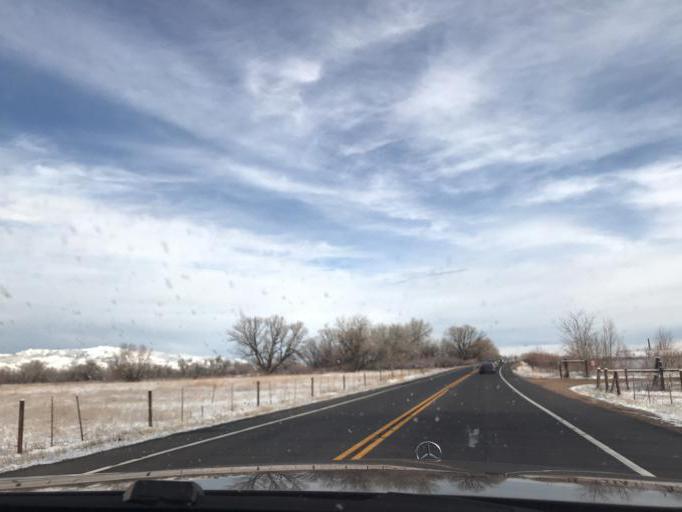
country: US
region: Colorado
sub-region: Boulder County
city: Superior
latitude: 39.9892
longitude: -105.2128
